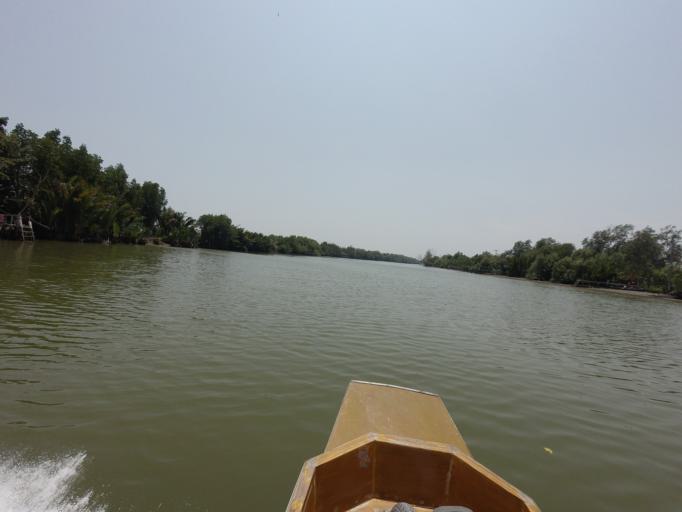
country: TH
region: Bangkok
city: Thung Khru
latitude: 13.5460
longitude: 100.4840
